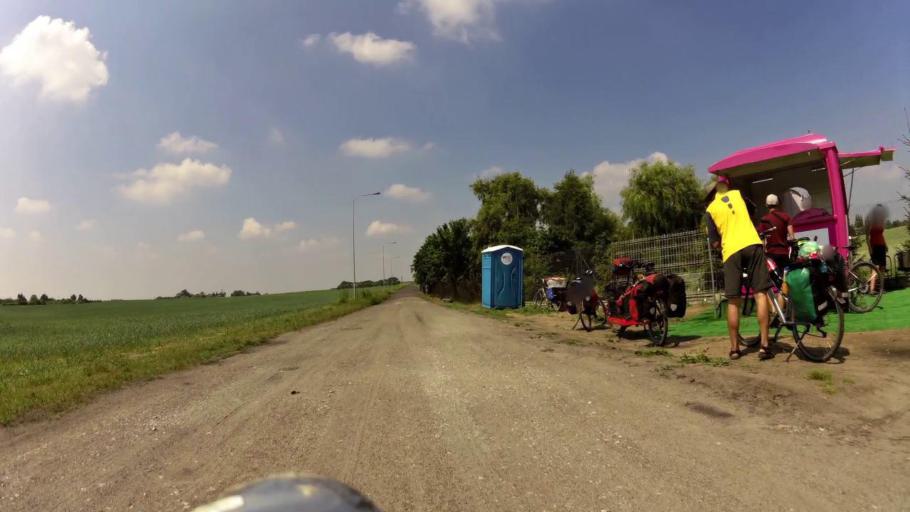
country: PL
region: Kujawsko-Pomorskie
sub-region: Powiat bydgoski
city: Koronowo
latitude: 53.2806
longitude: 17.9349
